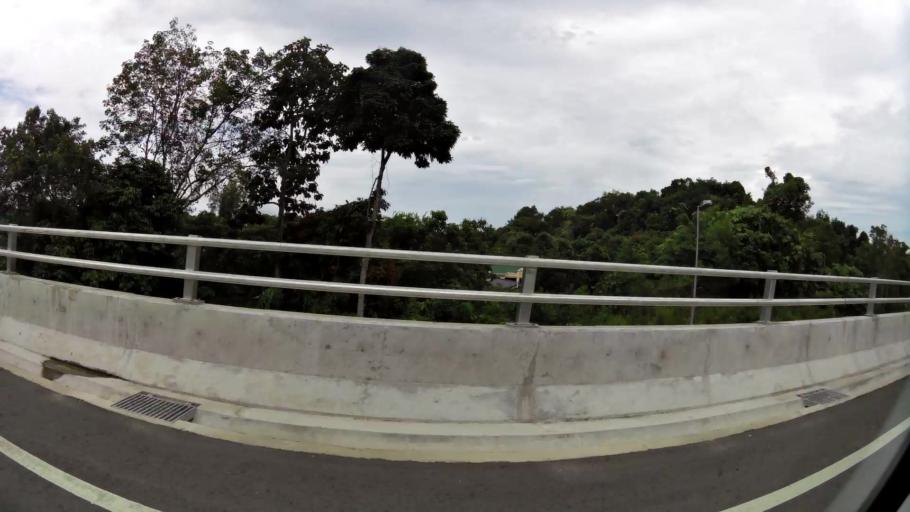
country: BN
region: Brunei and Muara
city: Bandar Seri Begawan
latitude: 4.8811
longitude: 114.9213
